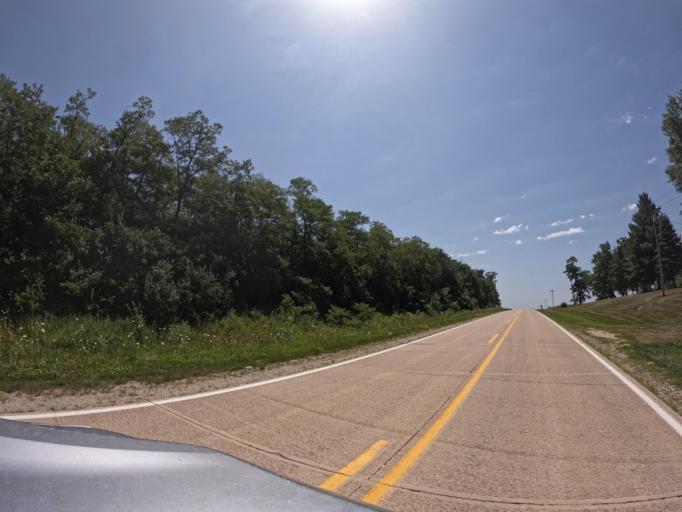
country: US
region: Iowa
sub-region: Henry County
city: Mount Pleasant
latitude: 40.9147
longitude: -91.5544
